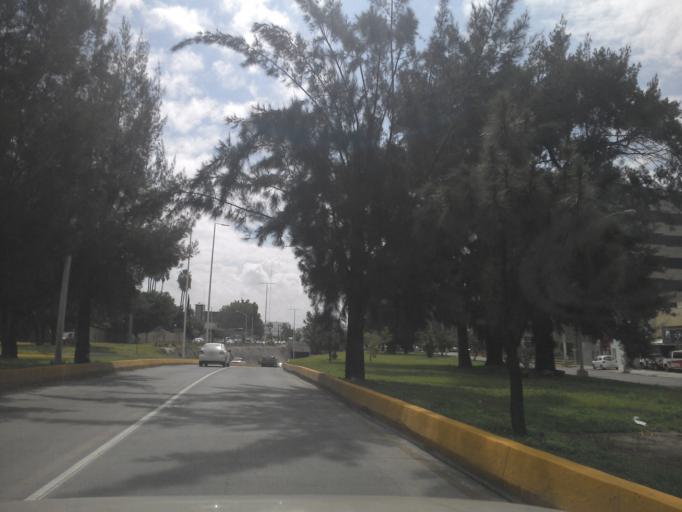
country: MX
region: Jalisco
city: Guadalajara
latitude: 20.6744
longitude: -103.4118
